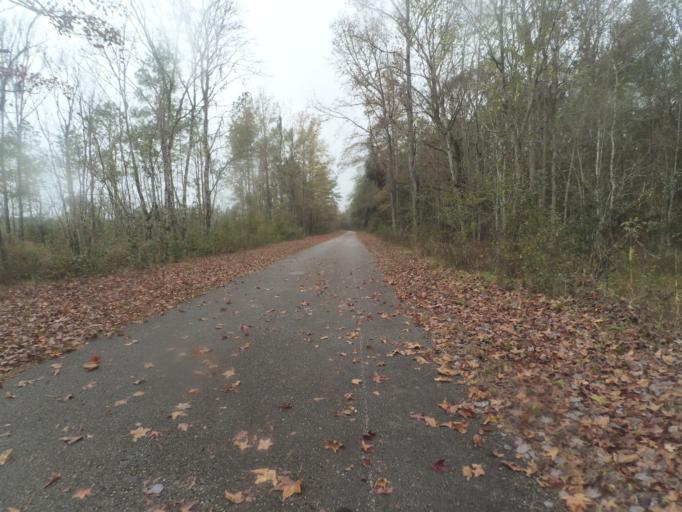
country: US
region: Florida
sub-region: Alachua County
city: Hawthorne
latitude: 29.5965
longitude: -82.1652
